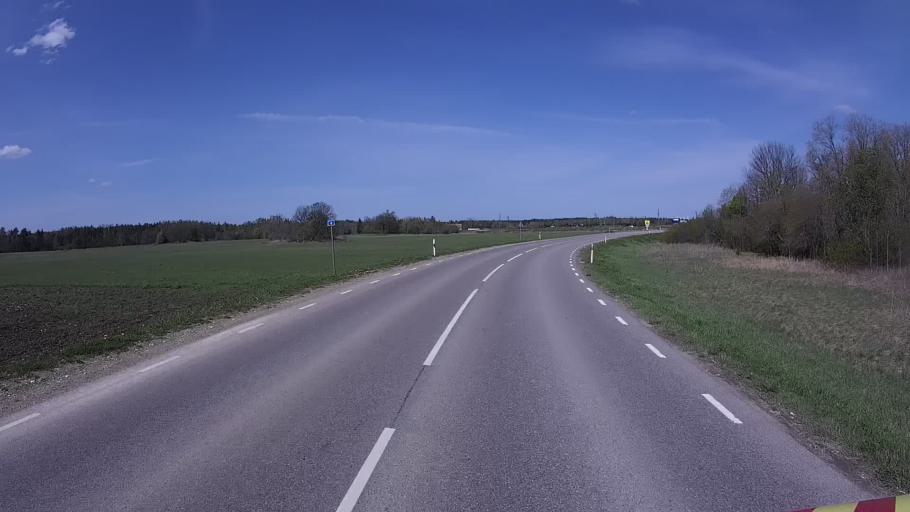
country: EE
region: Harju
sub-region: Keila linn
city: Keila
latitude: 59.3115
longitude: 24.3175
